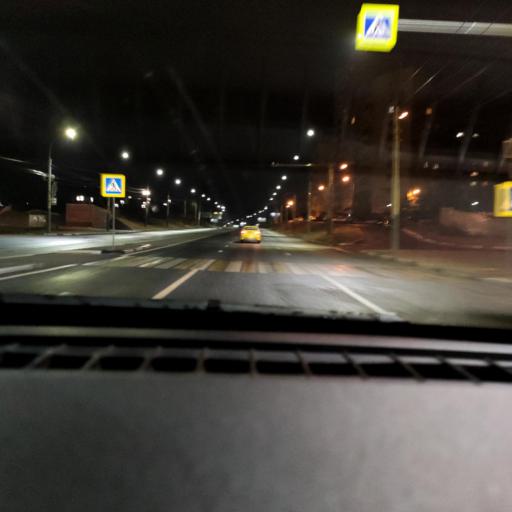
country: RU
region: Voronezj
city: Voronezh
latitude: 51.6403
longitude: 39.2049
